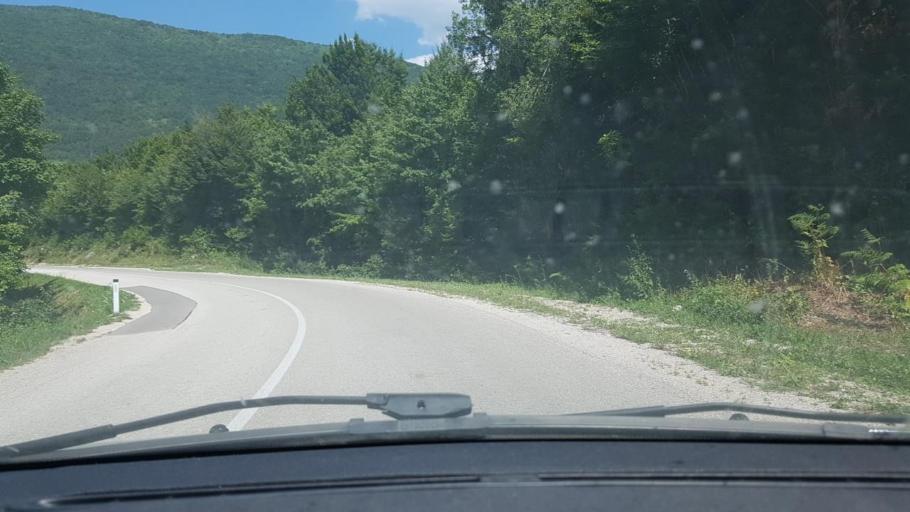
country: BA
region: Federation of Bosnia and Herzegovina
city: Orasac
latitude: 44.7105
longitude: 16.0368
